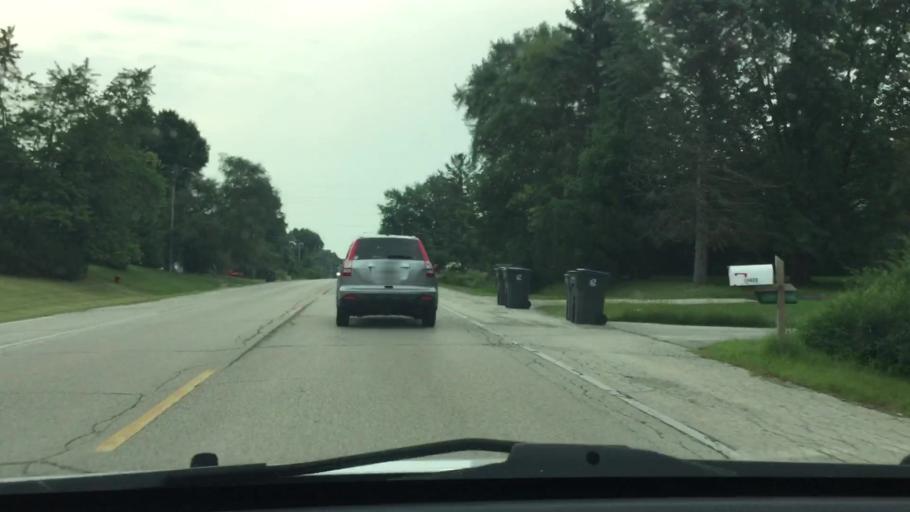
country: US
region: Wisconsin
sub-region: Waukesha County
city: New Berlin
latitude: 42.9955
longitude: -88.0818
